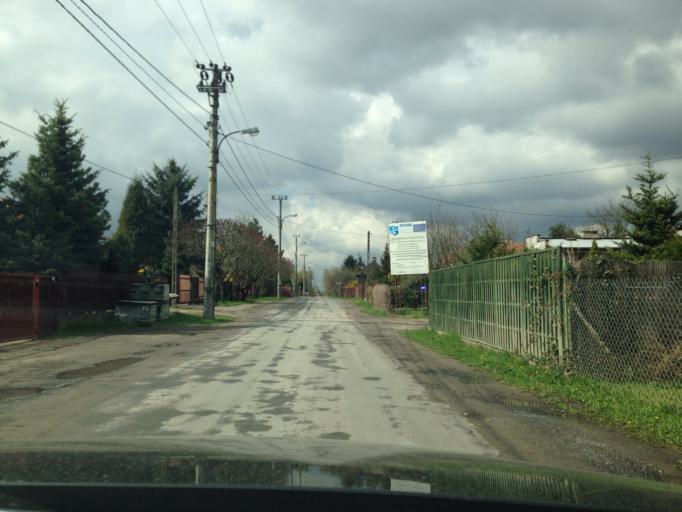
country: PL
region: Masovian Voivodeship
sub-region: Powiat warszawski zachodni
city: Babice
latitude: 52.2600
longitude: 20.8527
